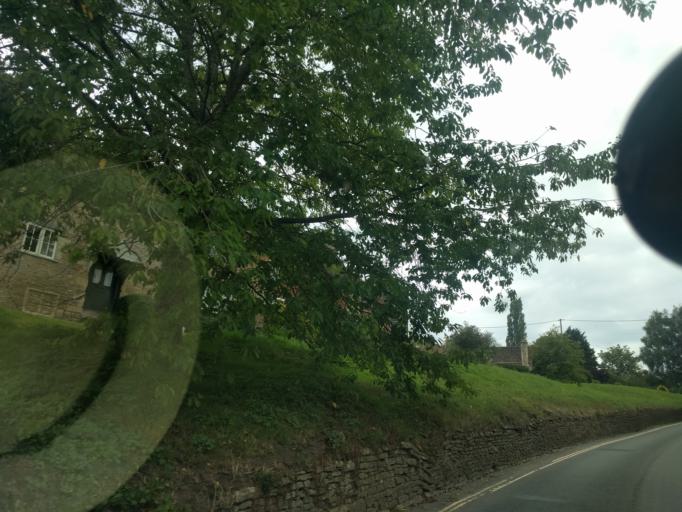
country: GB
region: England
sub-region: Wiltshire
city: Lacock
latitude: 51.4144
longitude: -2.1231
